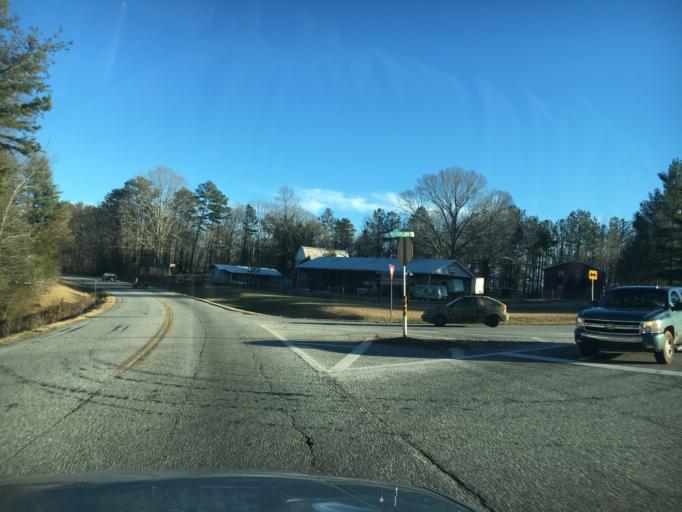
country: US
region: Georgia
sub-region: Habersham County
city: Demorest
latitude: 34.5523
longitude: -83.5717
